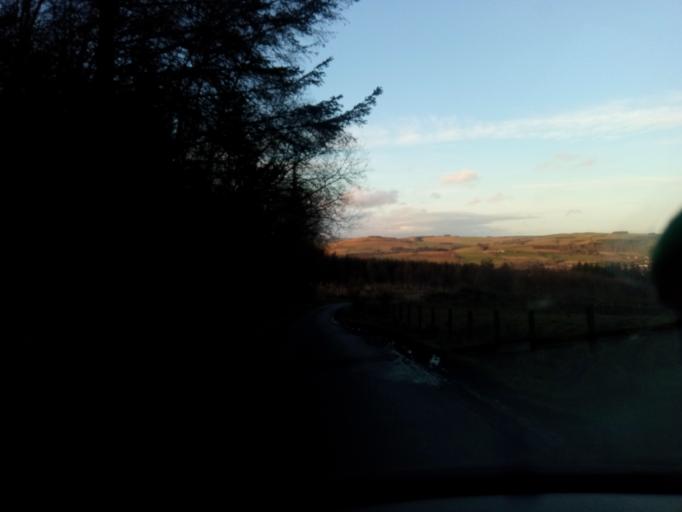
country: GB
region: Scotland
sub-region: The Scottish Borders
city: Melrose
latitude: 55.5832
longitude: -2.7402
